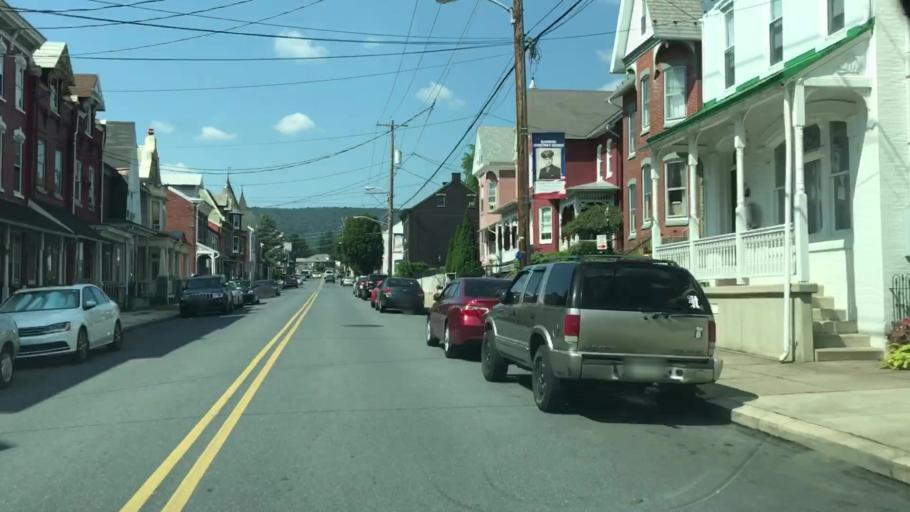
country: US
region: Pennsylvania
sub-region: Berks County
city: Hamburg
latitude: 40.5562
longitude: -75.9827
